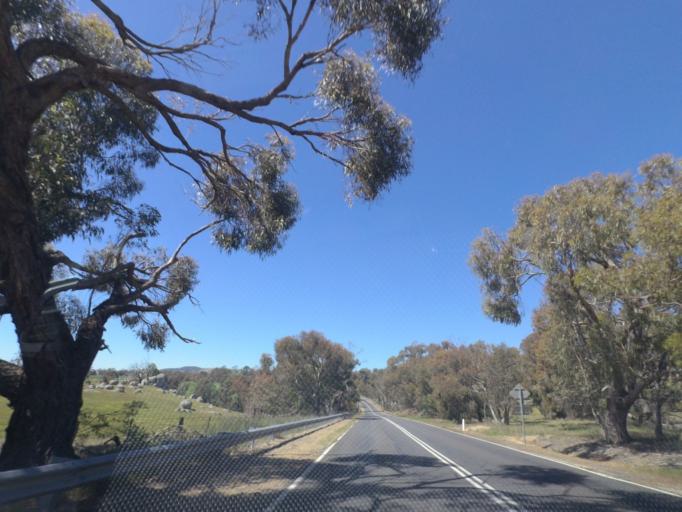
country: AU
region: Victoria
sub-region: Hume
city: Sunbury
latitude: -37.0718
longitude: 144.7746
